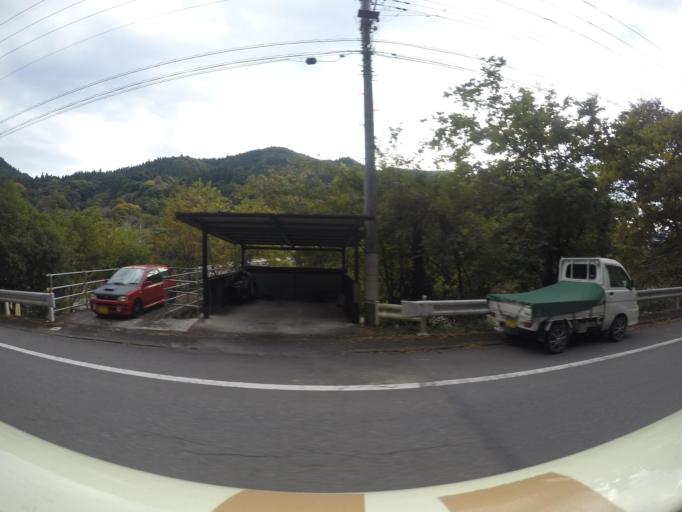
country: JP
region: Gunma
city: Tomioka
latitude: 36.1158
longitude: 138.9221
